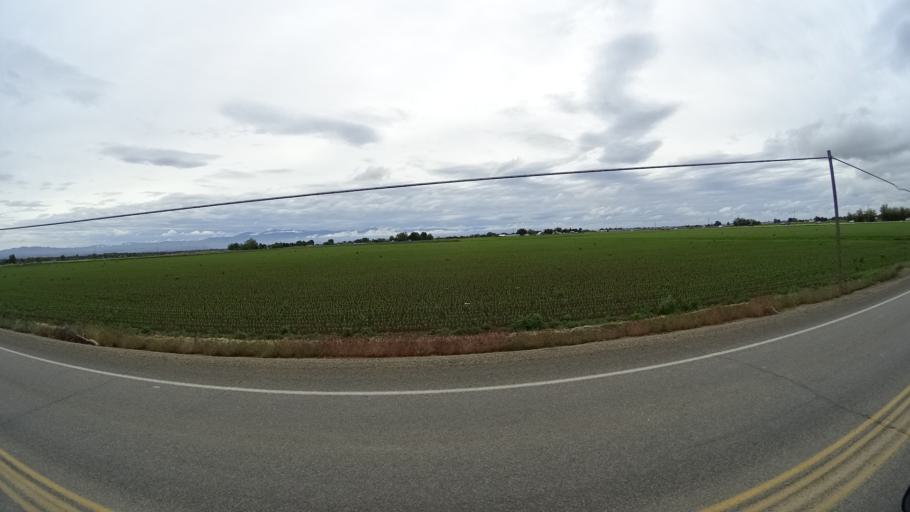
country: US
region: Idaho
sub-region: Ada County
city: Star
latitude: 43.6654
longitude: -116.4934
